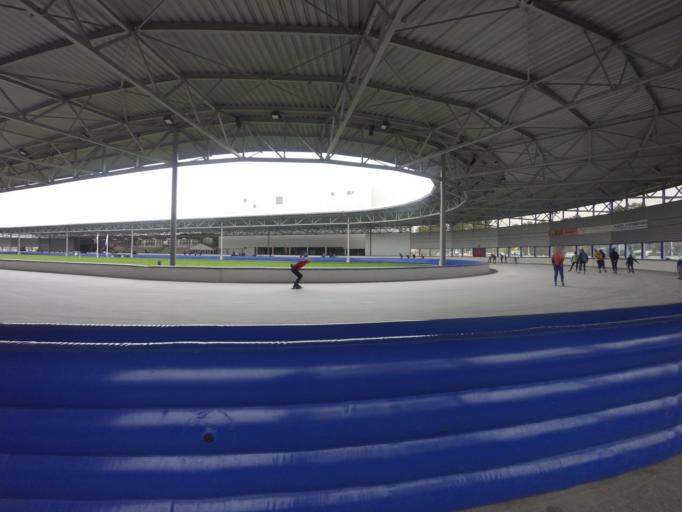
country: NL
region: North Holland
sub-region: Gemeente Alkmaar
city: Alkmaar
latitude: 52.6324
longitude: 4.7129
